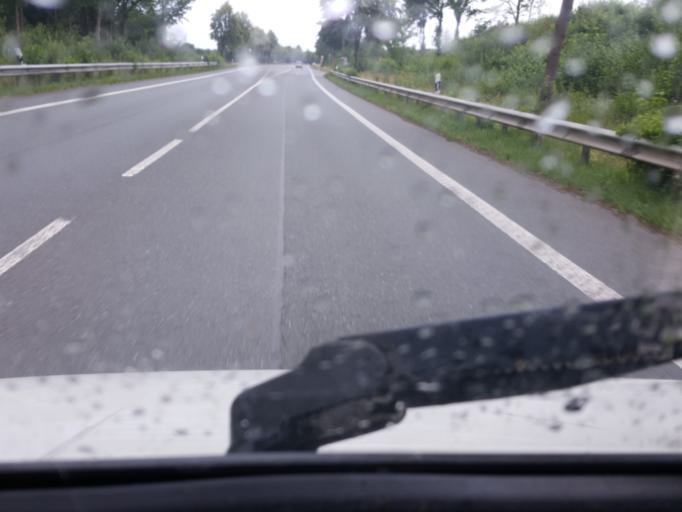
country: DE
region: North Rhine-Westphalia
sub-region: Regierungsbezirk Detmold
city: Petershagen
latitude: 52.3698
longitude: 8.9559
